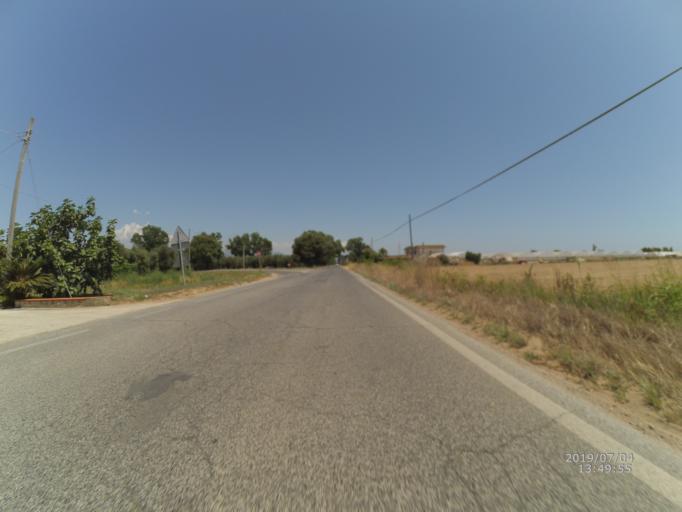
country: IT
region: Latium
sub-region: Provincia di Latina
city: San Felice Circeo
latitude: 41.2856
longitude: 13.1196
